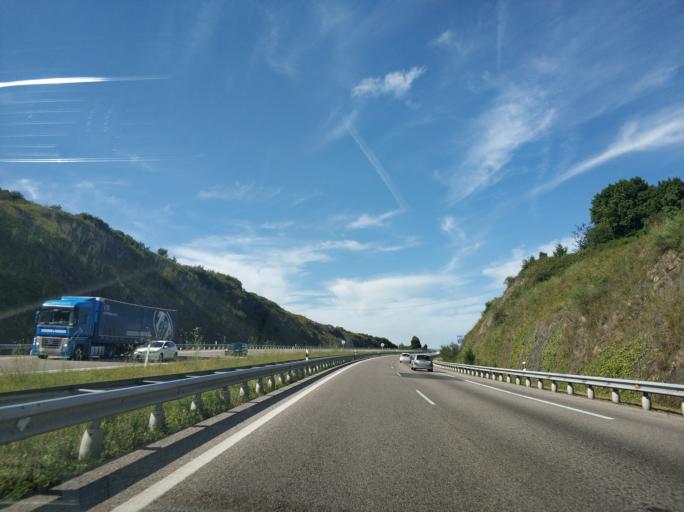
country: ES
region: Asturias
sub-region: Province of Asturias
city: Soto del Barco
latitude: 43.5267
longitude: -6.0557
